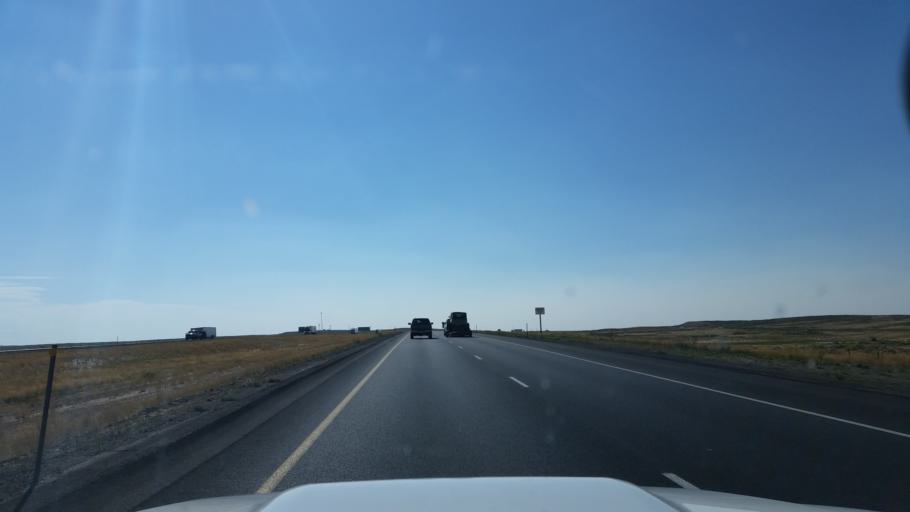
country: US
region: Wyoming
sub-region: Sweetwater County
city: Green River
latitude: 41.5420
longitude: -109.8781
